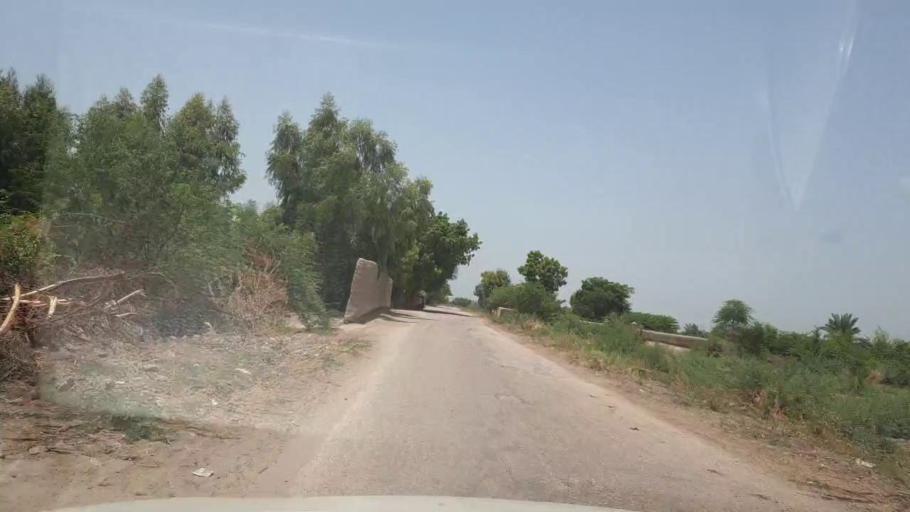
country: PK
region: Sindh
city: Bozdar
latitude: 27.1860
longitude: 68.6206
